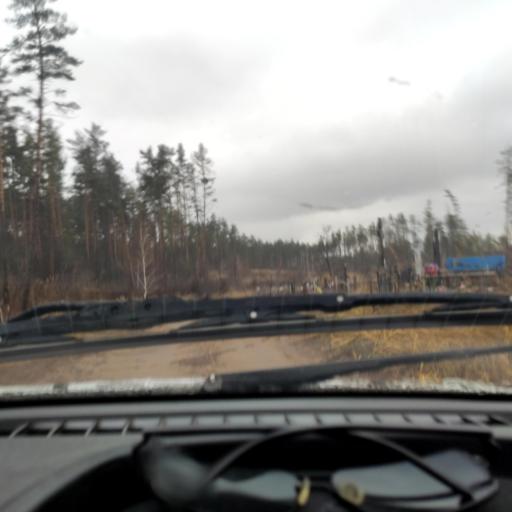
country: RU
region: Samara
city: Zhigulevsk
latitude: 53.5376
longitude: 49.5547
